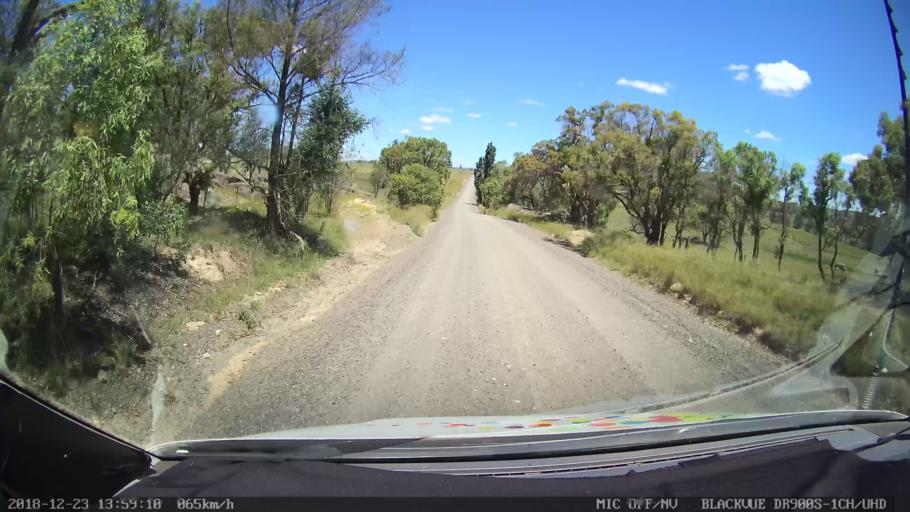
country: AU
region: New South Wales
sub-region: Tamworth Municipality
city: Manilla
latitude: -30.6053
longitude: 151.0952
